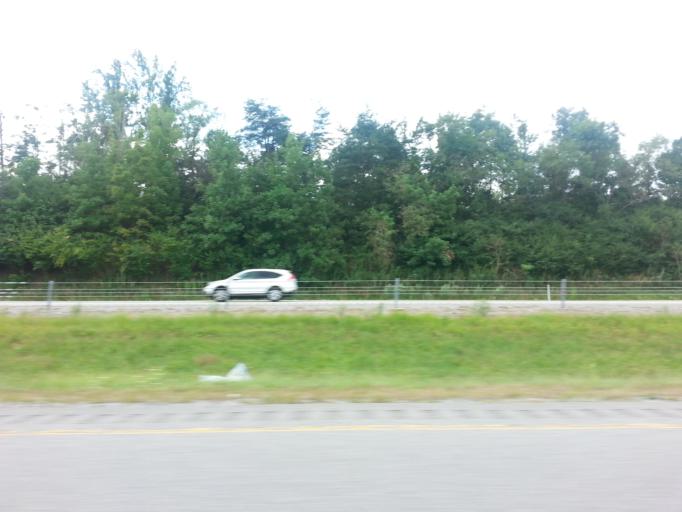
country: US
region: Tennessee
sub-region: Putnam County
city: Monterey
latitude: 36.1405
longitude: -85.2743
